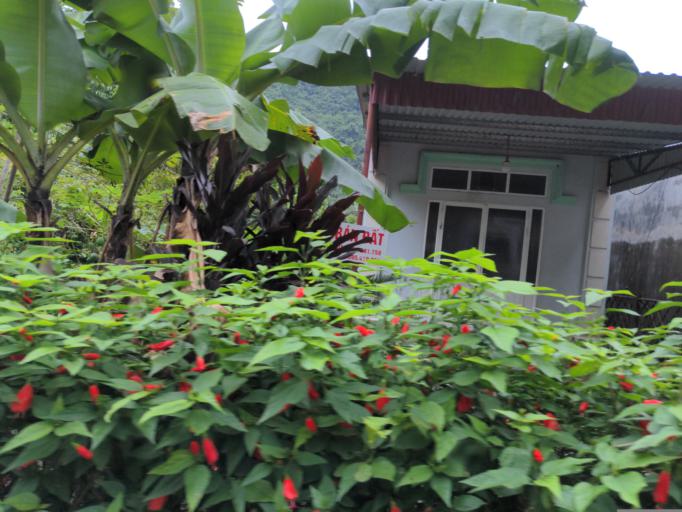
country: VN
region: Hai Phong
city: Cat Ba
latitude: 20.7984
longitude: 107.0429
